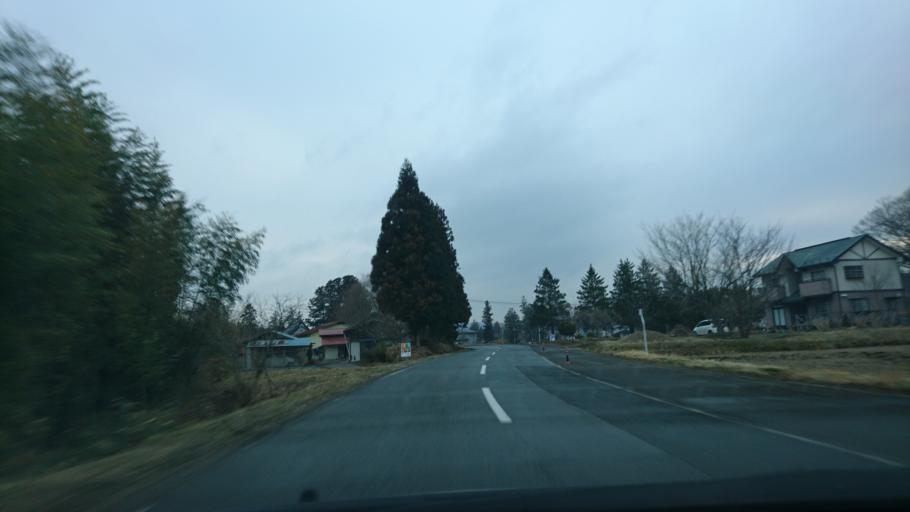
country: JP
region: Iwate
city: Ichinoseki
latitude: 39.0169
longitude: 141.3525
